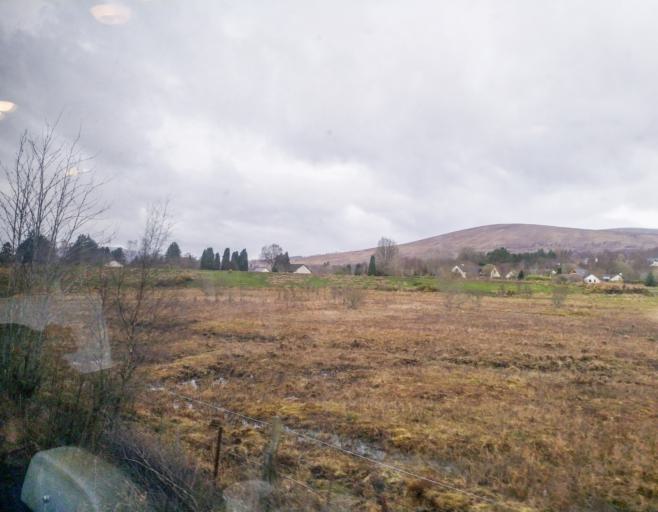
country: GB
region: Scotland
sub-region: Highland
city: Spean Bridge
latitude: 56.8881
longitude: -4.8558
